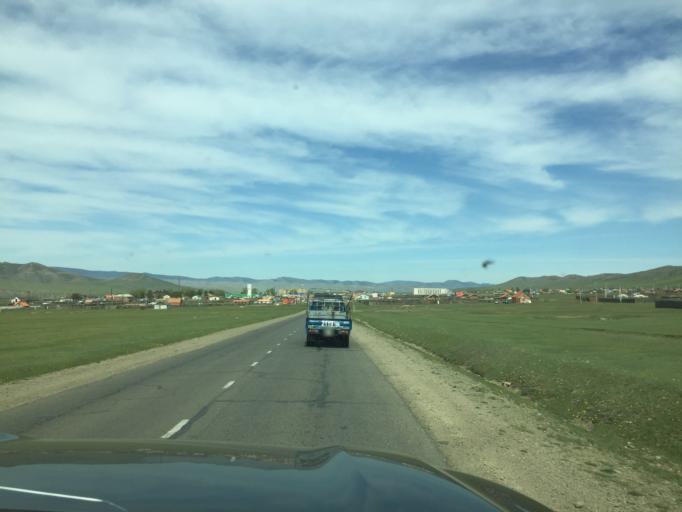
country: MN
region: Central Aimak
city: Ihsueuej
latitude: 48.2184
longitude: 106.3037
